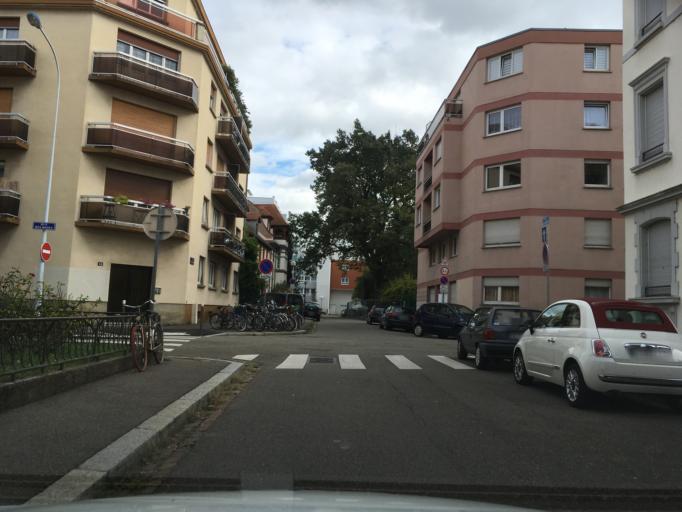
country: FR
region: Alsace
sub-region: Departement du Bas-Rhin
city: Strasbourg
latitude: 48.5693
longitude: 7.7596
